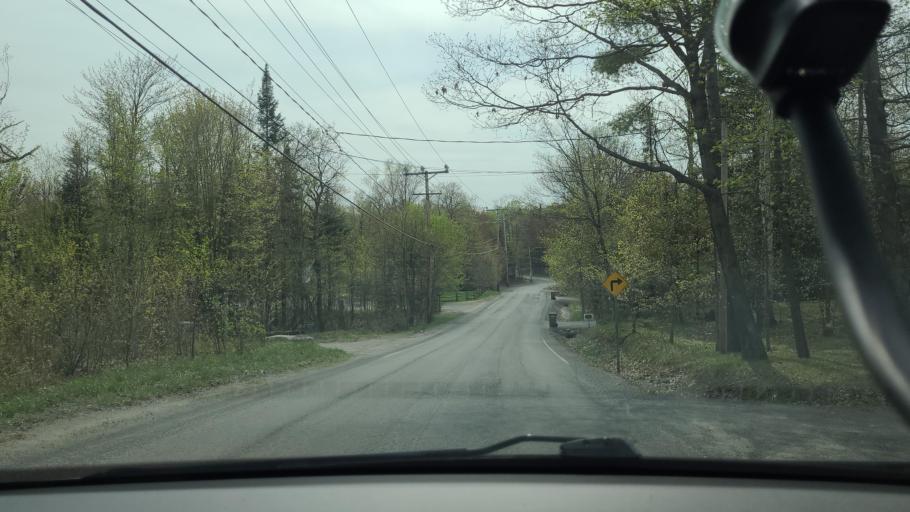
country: CA
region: Quebec
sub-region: Laurentides
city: Prevost
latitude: 45.8912
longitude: -74.0484
